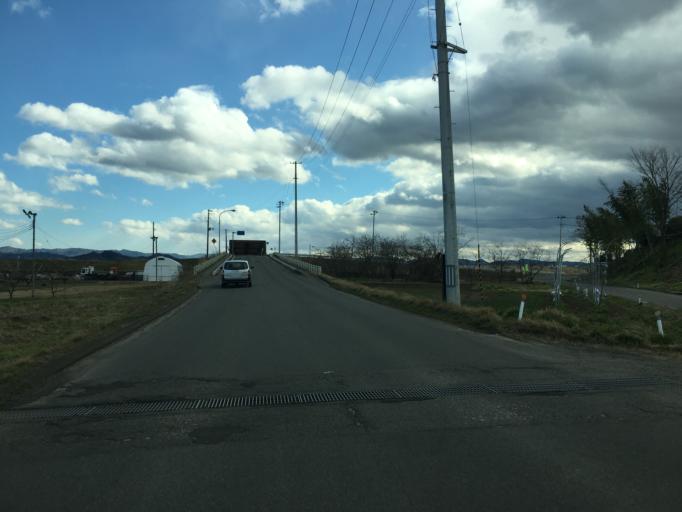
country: JP
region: Fukushima
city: Yanagawamachi-saiwaicho
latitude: 37.8651
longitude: 140.5683
